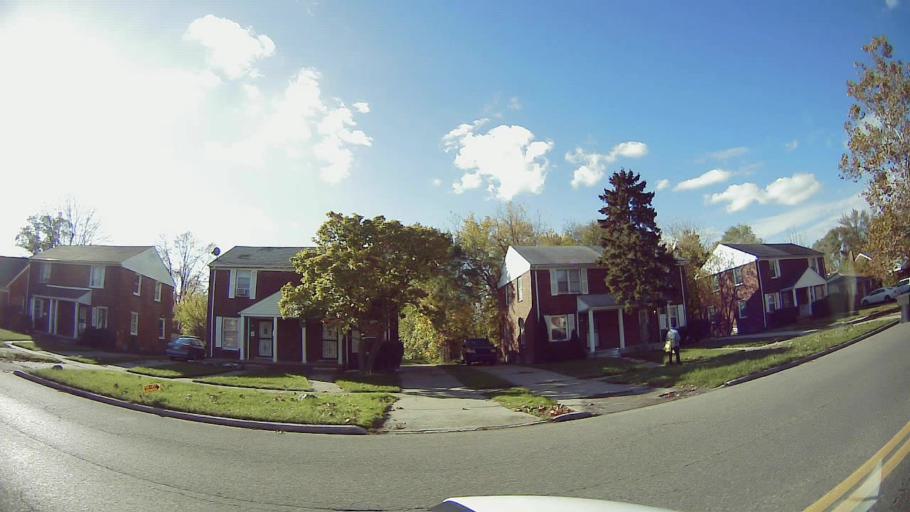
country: US
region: Michigan
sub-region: Wayne County
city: Dearborn Heights
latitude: 42.3605
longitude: -83.2360
